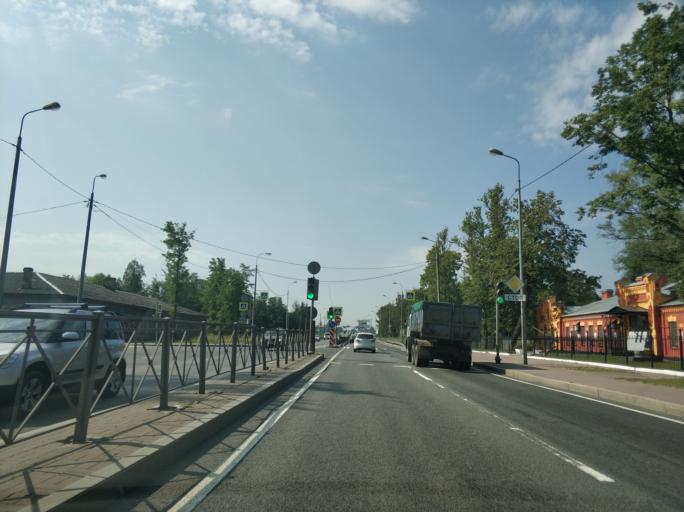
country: RU
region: St.-Petersburg
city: Krasnogvargeisky
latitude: 59.9883
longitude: 30.5247
